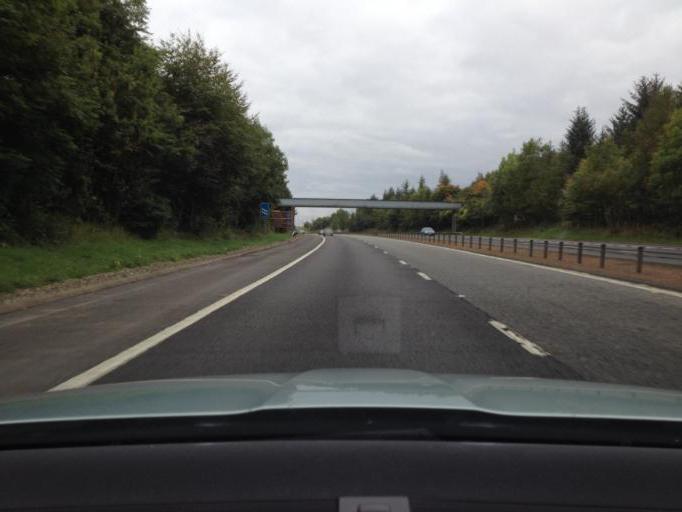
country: GB
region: Scotland
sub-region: Fife
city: Kelty
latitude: 56.1353
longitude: -3.3974
